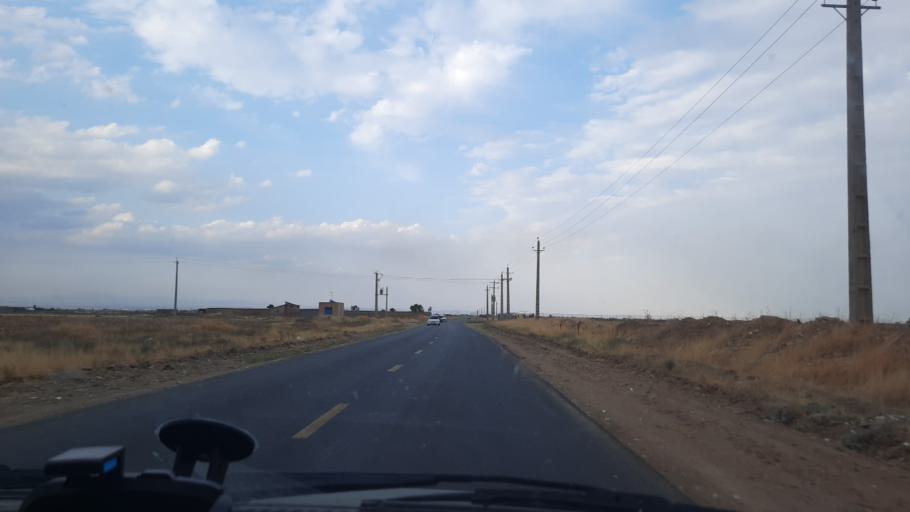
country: IR
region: Markazi
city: Arak
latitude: 34.1292
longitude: 49.7369
